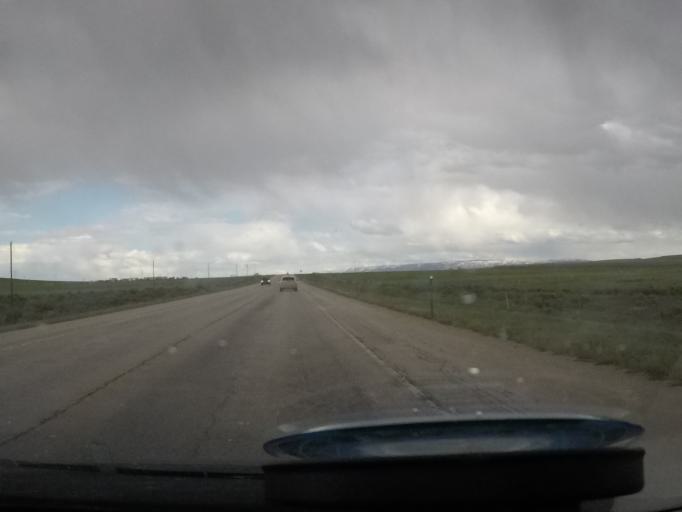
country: US
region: Wyoming
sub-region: Natrona County
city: Mills
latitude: 42.9581
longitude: -106.6540
